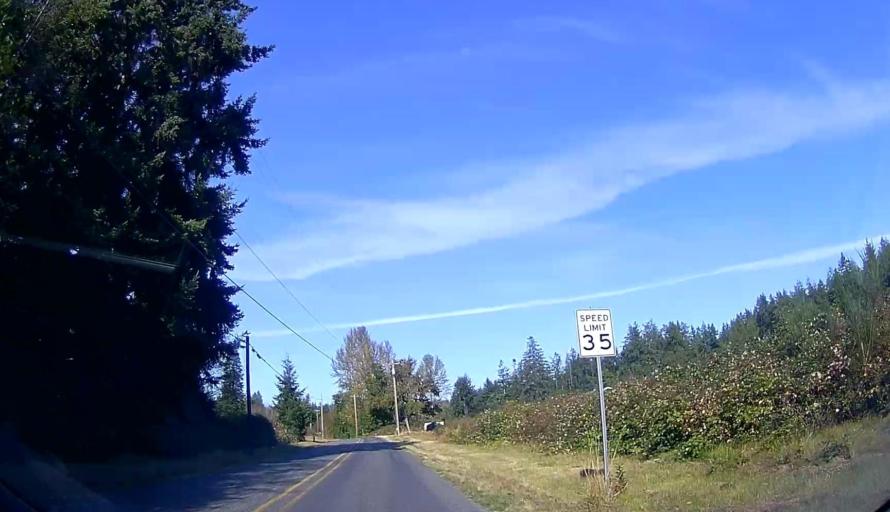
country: US
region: Washington
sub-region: Island County
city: Camano
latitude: 48.1787
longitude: -122.5193
